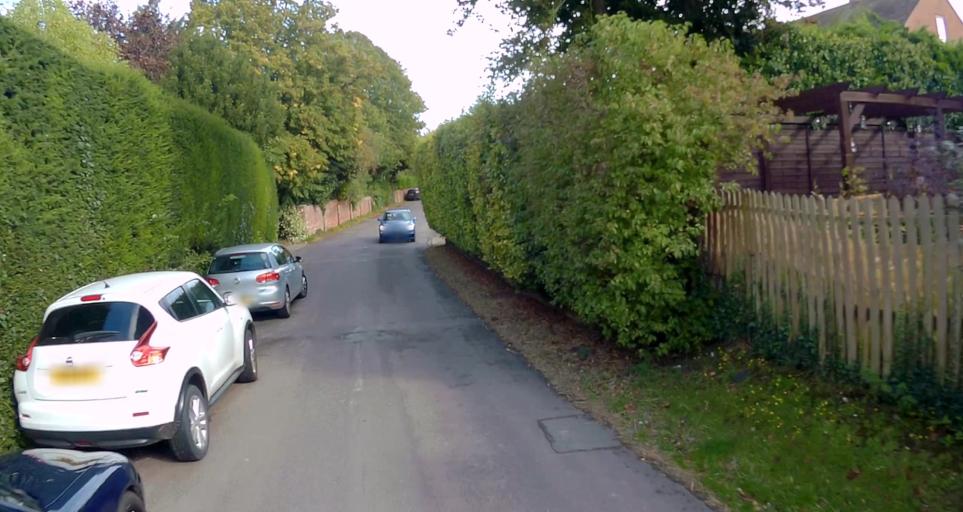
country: GB
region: England
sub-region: Hampshire
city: Kings Worthy
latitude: 51.0858
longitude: -1.2709
